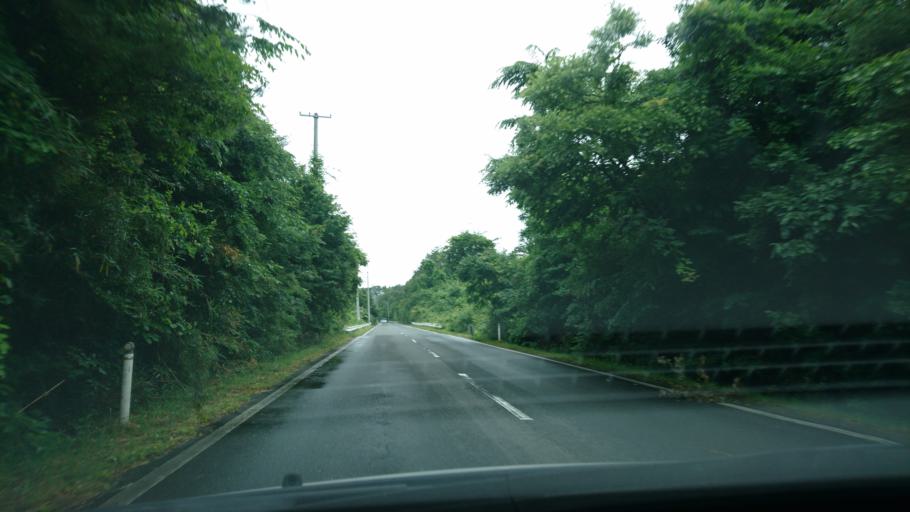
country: JP
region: Iwate
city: Ichinoseki
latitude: 38.8894
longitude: 141.1496
